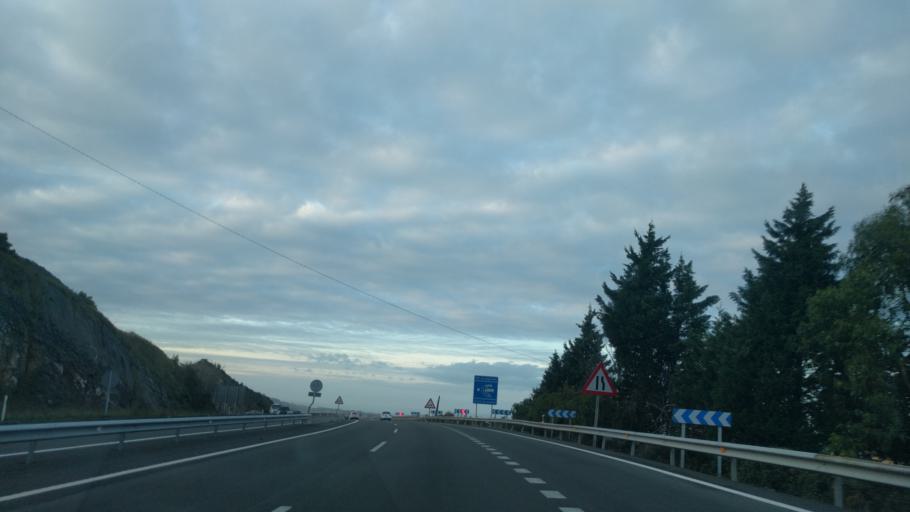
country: ES
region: Cantabria
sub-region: Provincia de Cantabria
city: Castro-Urdiales
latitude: 43.3603
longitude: -3.1861
